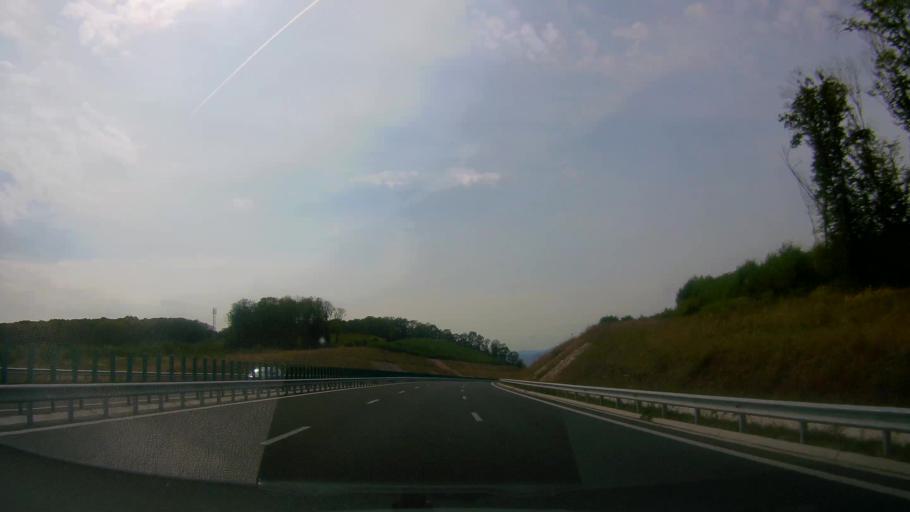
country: RO
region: Cluj
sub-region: Comuna Floresti
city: Luna de Sus
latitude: 46.7840
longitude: 23.4160
